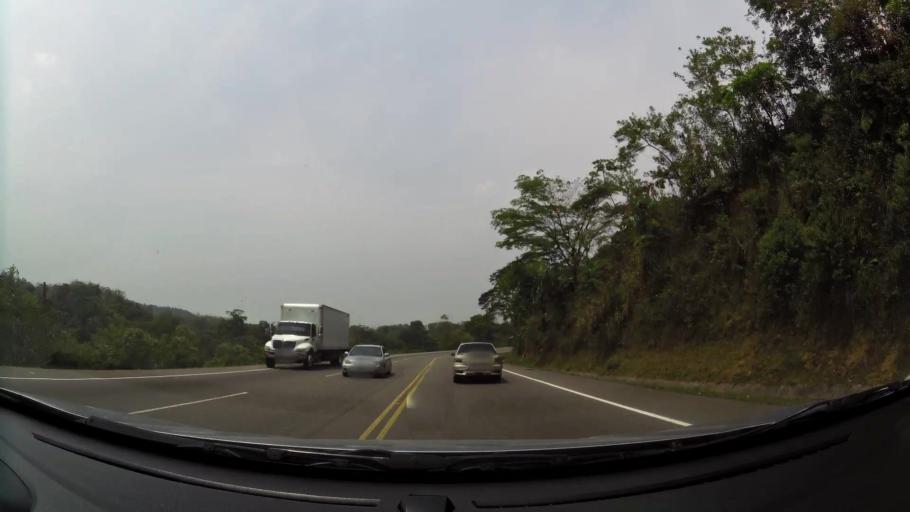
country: HN
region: Cortes
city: Santa Cruz de Yojoa
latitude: 14.9705
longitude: -87.9350
